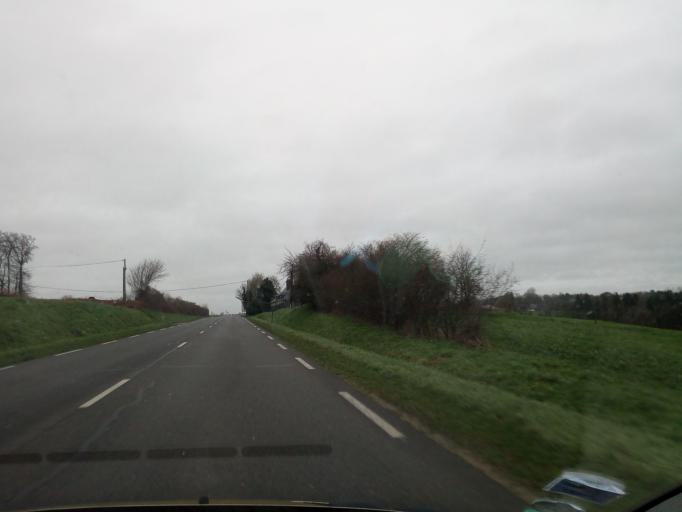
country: FR
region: Haute-Normandie
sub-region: Departement de la Seine-Maritime
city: Auzebosc
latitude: 49.5933
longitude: 0.7356
